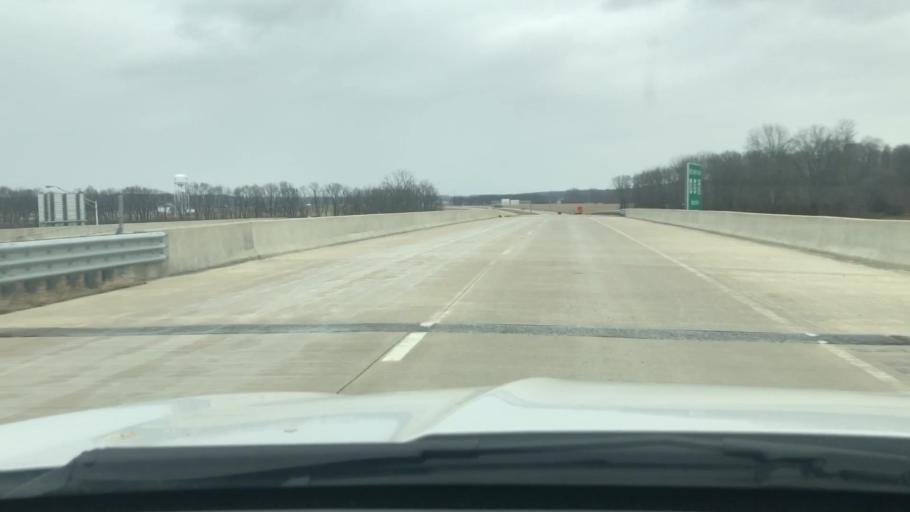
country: US
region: Indiana
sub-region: Cass County
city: Dunkirk
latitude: 40.7282
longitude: -86.3785
